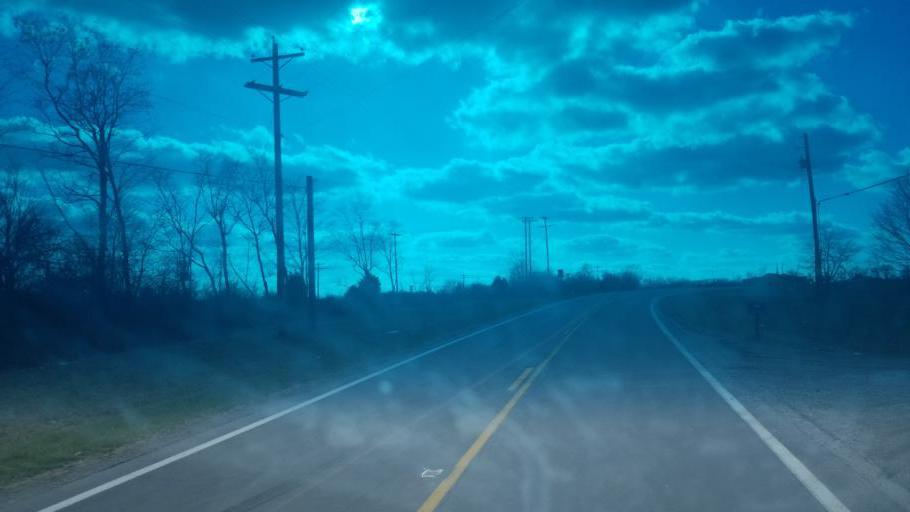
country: US
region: Ohio
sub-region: Highland County
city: Greenfield
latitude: 39.3458
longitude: -83.4174
